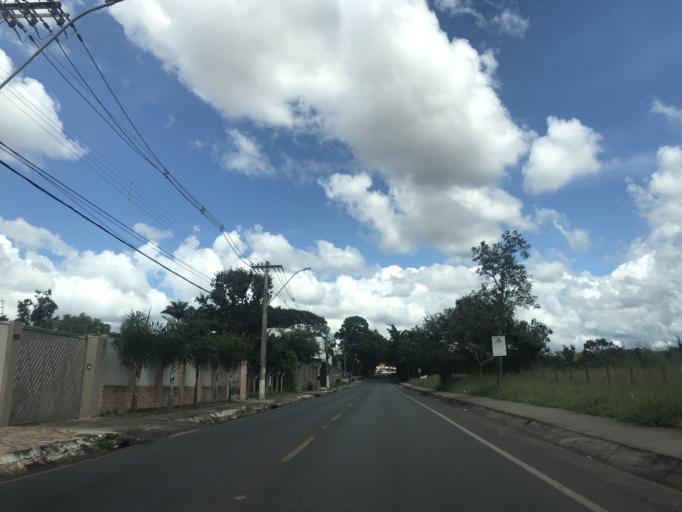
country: BR
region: Federal District
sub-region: Brasilia
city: Brasilia
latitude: -15.8778
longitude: -47.8041
